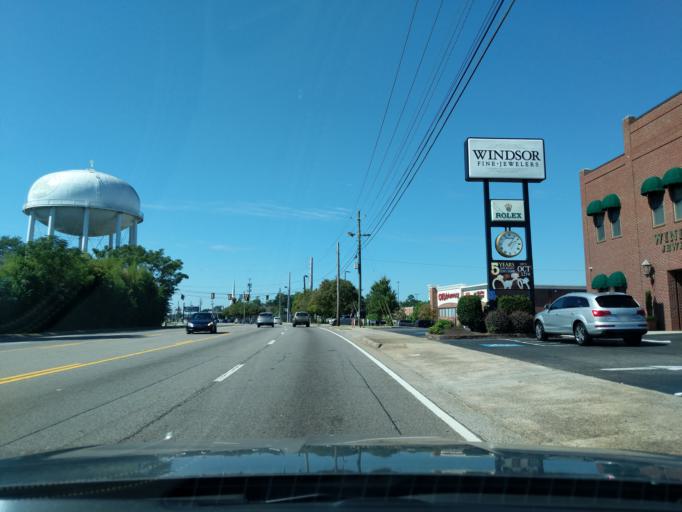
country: US
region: Georgia
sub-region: Columbia County
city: Martinez
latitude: 33.5079
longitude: -82.0214
